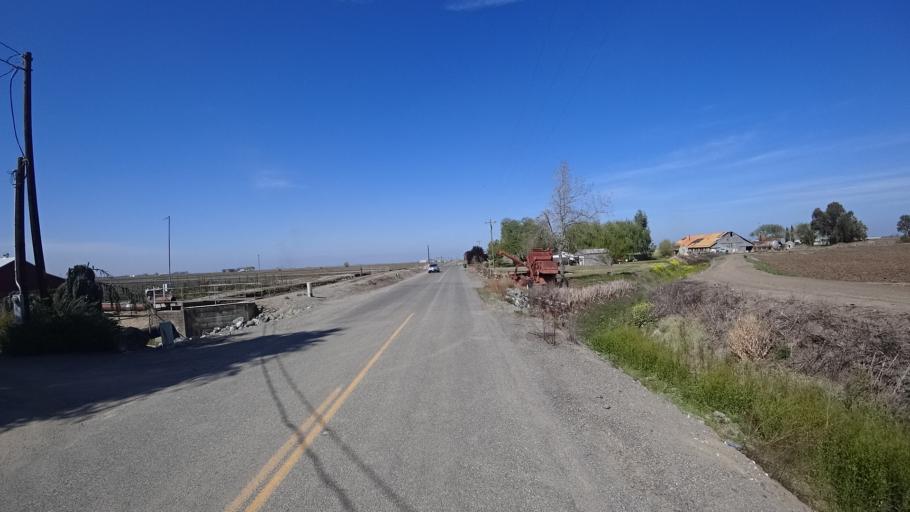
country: US
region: California
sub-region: Glenn County
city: Hamilton City
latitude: 39.6162
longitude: -122.0632
